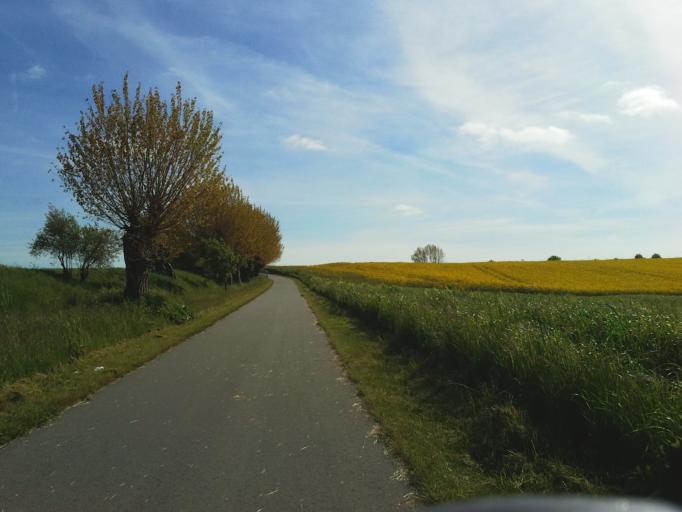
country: DE
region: Mecklenburg-Vorpommern
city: Schwaan
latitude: 53.9808
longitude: 12.1034
